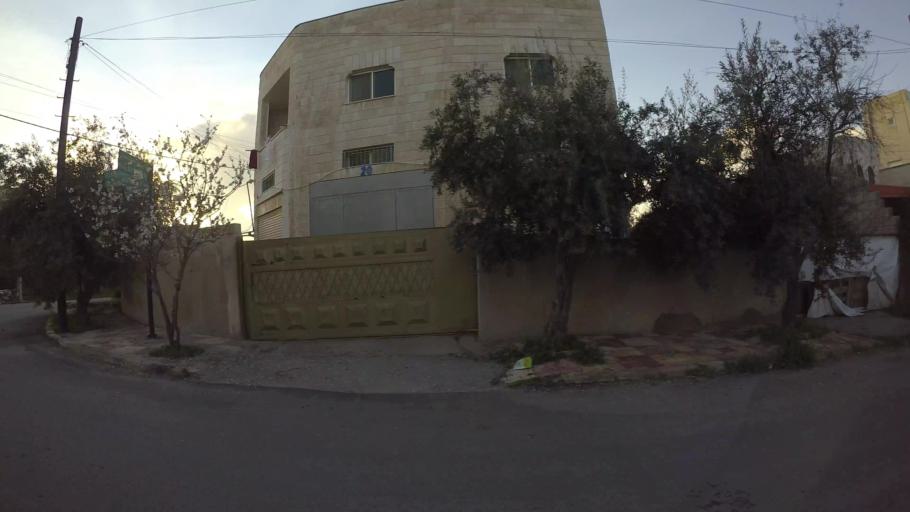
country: JO
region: Amman
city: Al Bunayyat ash Shamaliyah
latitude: 31.9051
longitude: 35.9060
